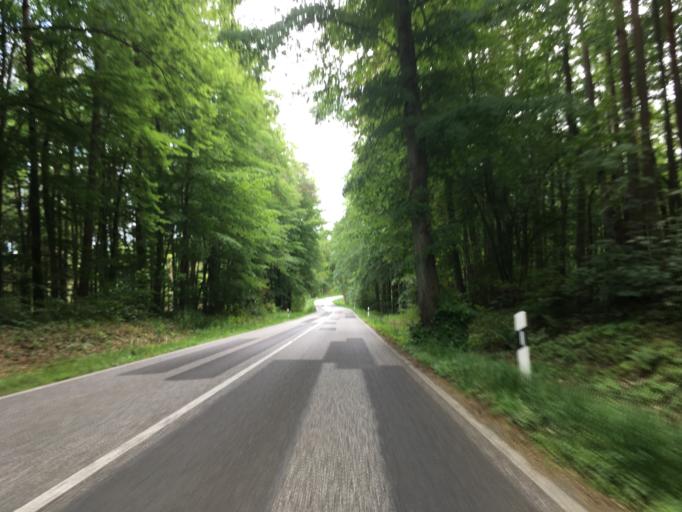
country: DE
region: Brandenburg
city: Bad Freienwalde
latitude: 52.7392
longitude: 13.9907
